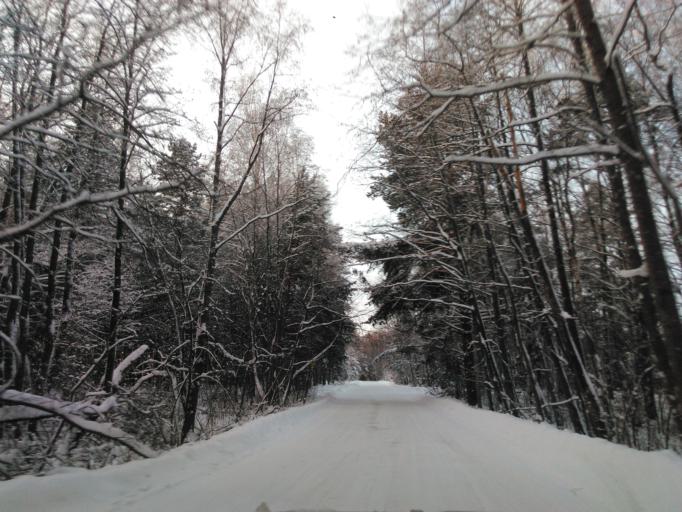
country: RU
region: Tverskaya
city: Konakovo
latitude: 56.6573
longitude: 36.6619
